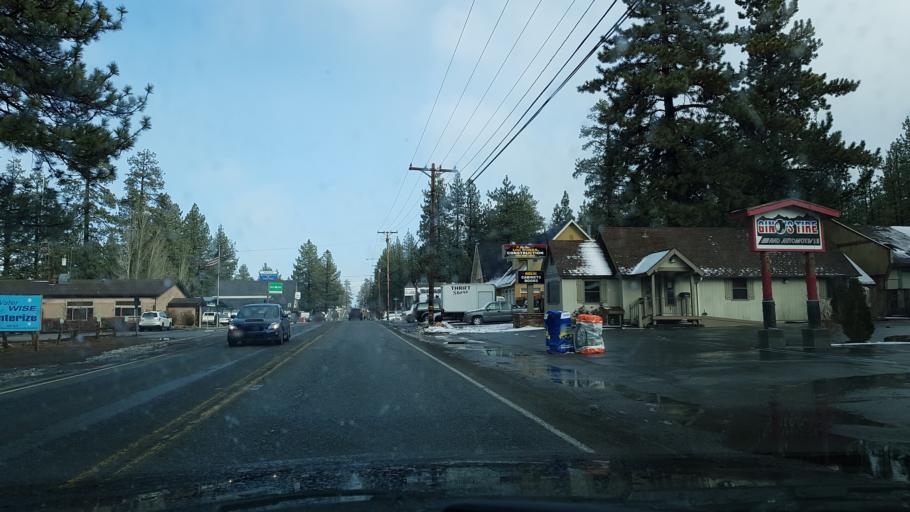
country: US
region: California
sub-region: San Bernardino County
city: Big Bear City
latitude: 34.2611
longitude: -116.8500
